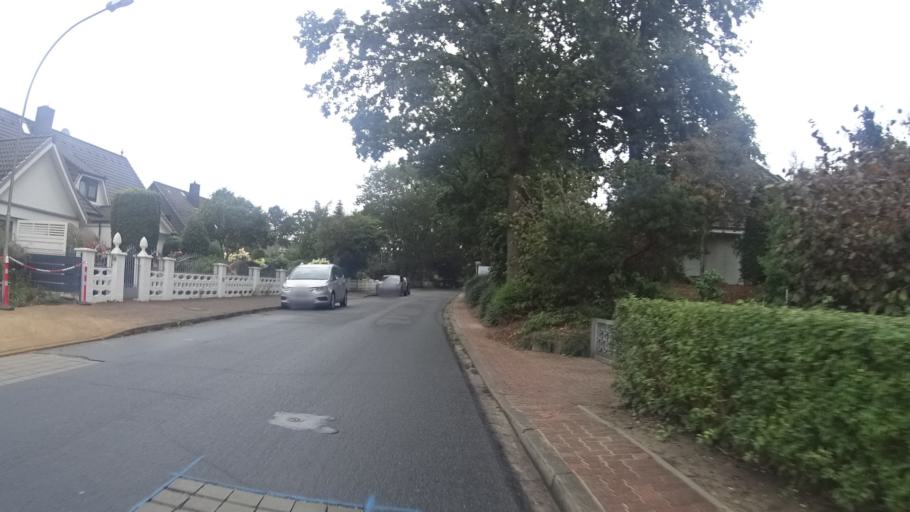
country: DE
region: Schleswig-Holstein
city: Kiebitzreihe
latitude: 53.7822
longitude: 9.6227
